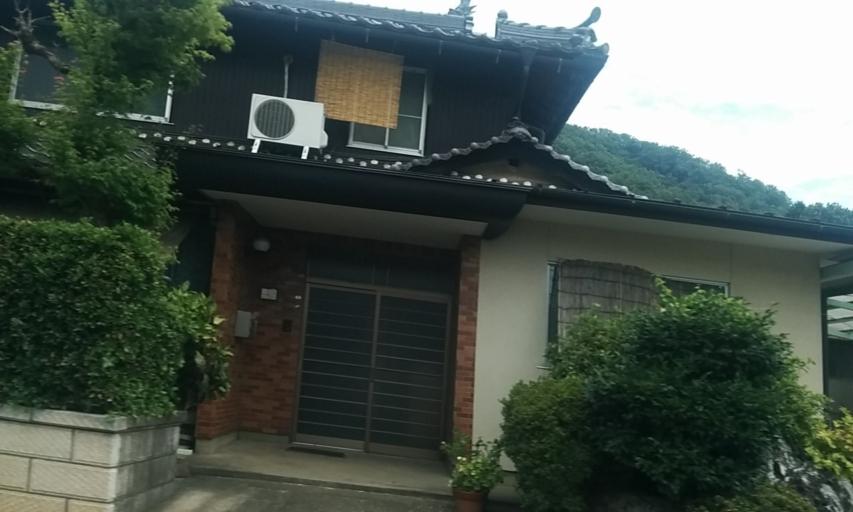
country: JP
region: Kyoto
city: Ayabe
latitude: 35.3420
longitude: 135.2166
